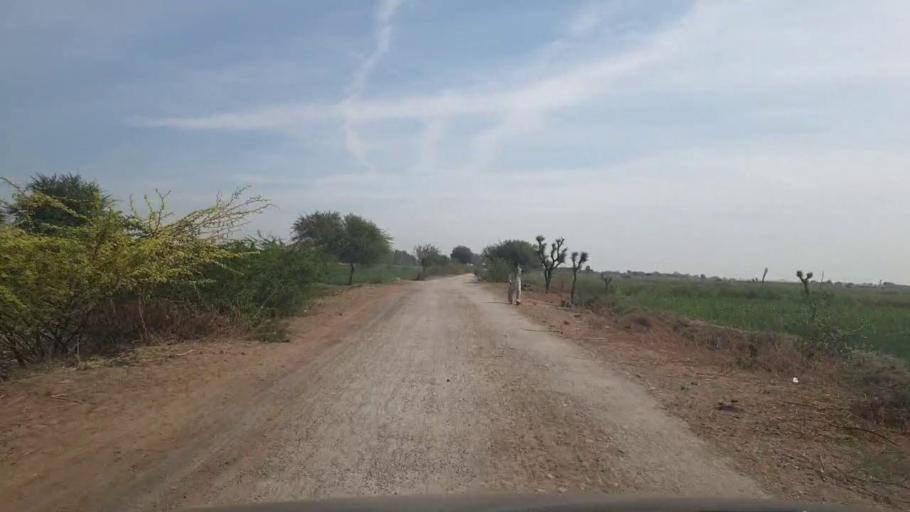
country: PK
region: Sindh
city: Umarkot
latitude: 25.3344
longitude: 69.5999
